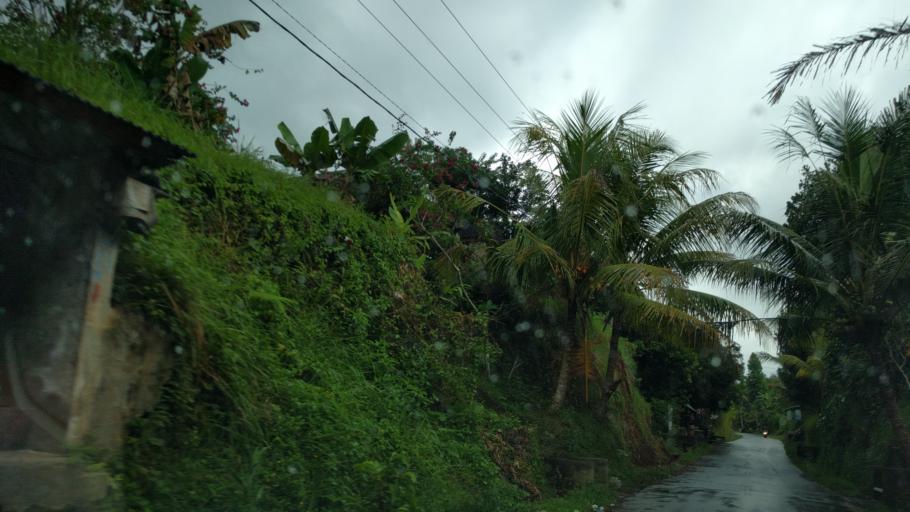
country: ID
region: Bali
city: Bunutan
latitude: -8.4728
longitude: 115.2599
